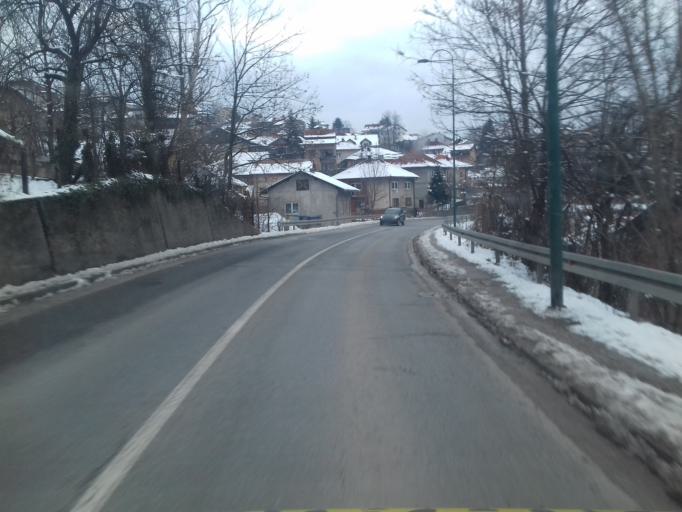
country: BA
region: Federation of Bosnia and Herzegovina
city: Kobilja Glava
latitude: 43.8519
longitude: 18.4297
